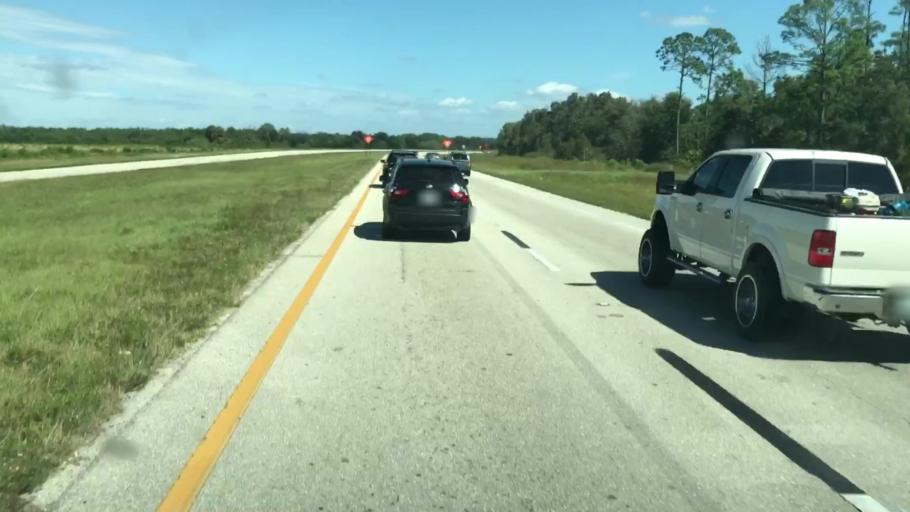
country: US
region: Florida
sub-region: Lee County
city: Gateway
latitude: 26.5743
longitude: -81.7232
